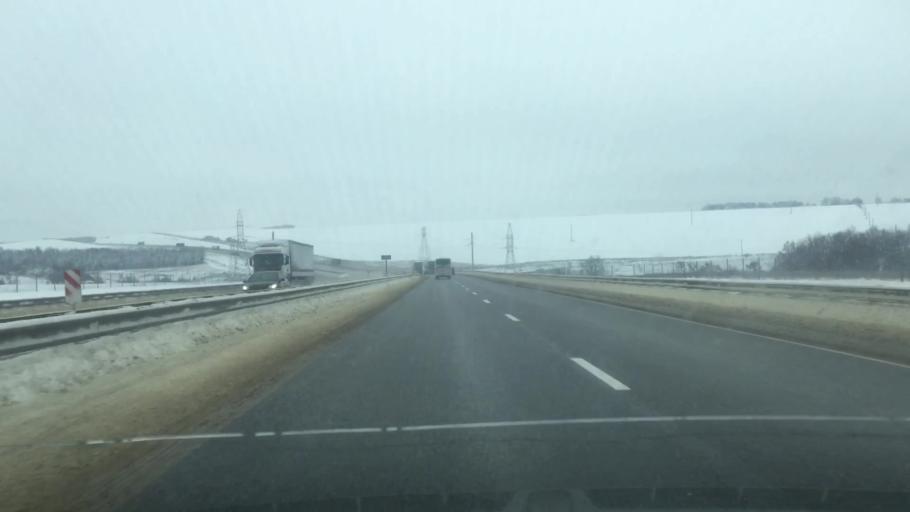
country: RU
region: Tula
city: Kazachka
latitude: 53.2801
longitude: 38.1797
